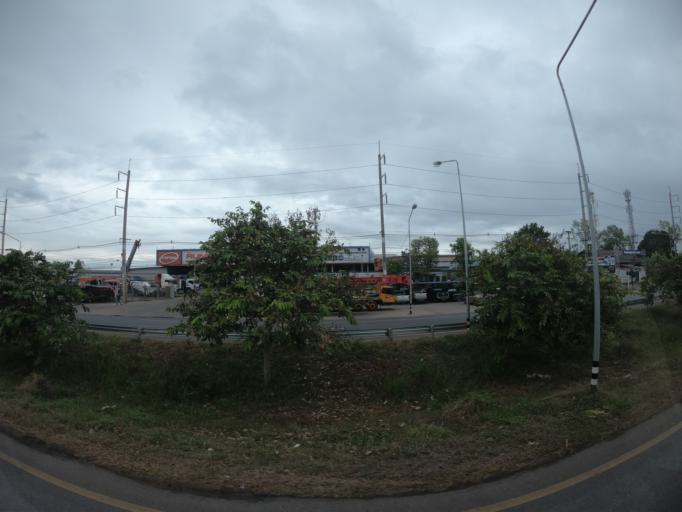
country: TH
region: Roi Et
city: Roi Et
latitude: 16.0489
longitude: 103.6212
